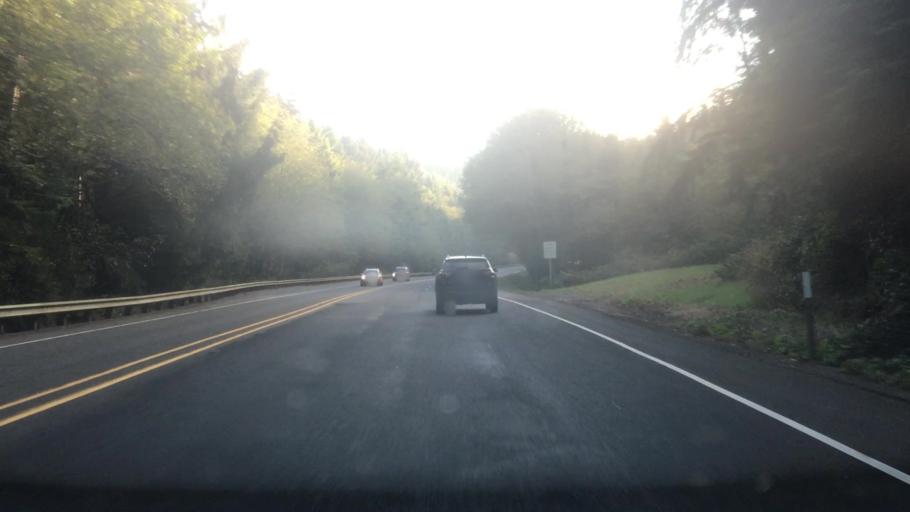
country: US
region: Oregon
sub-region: Clatsop County
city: Cannon Beach
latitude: 45.9266
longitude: -123.9298
